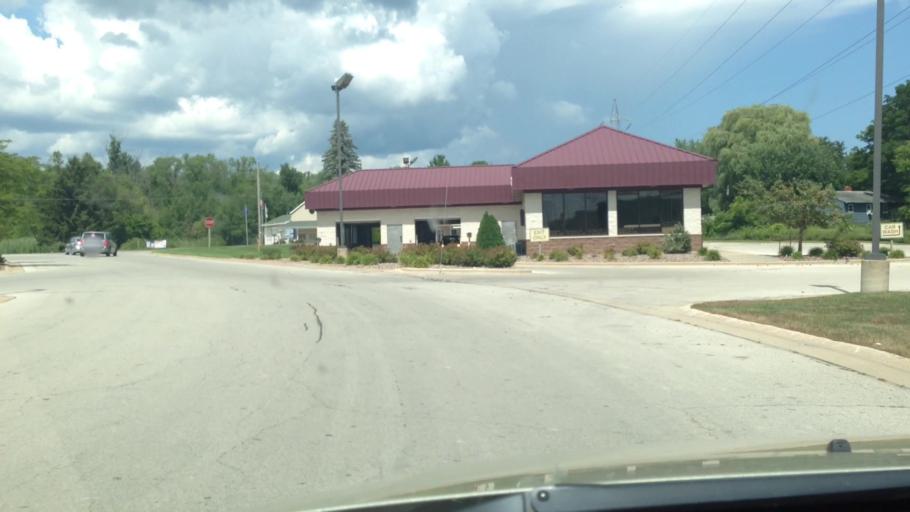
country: US
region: Wisconsin
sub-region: Brown County
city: Suamico
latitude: 44.6348
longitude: -88.0433
